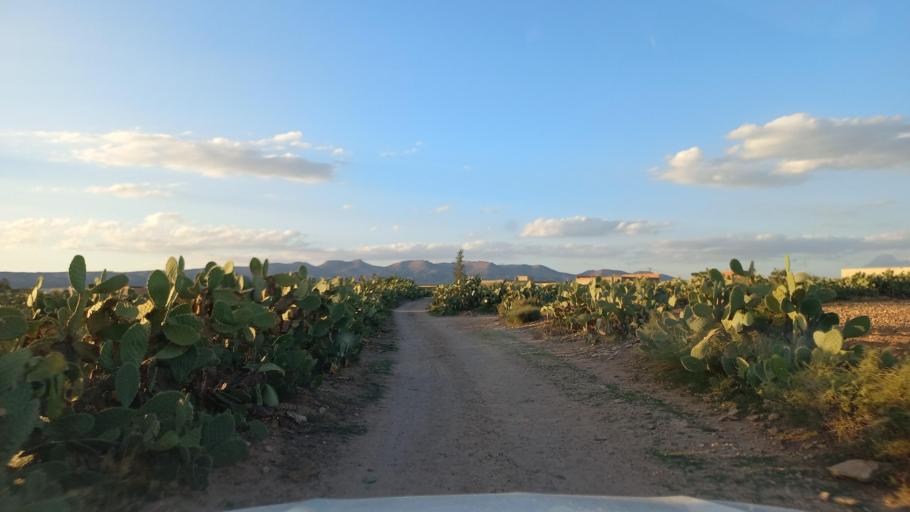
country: TN
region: Al Qasrayn
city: Sbiba
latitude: 35.3740
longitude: 9.0557
